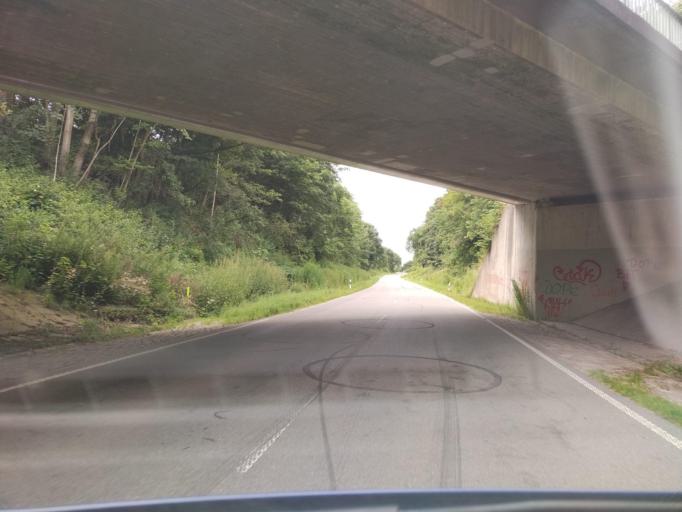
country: DE
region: Schleswig-Holstein
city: Fahrdorf
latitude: 54.5209
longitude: 9.5926
